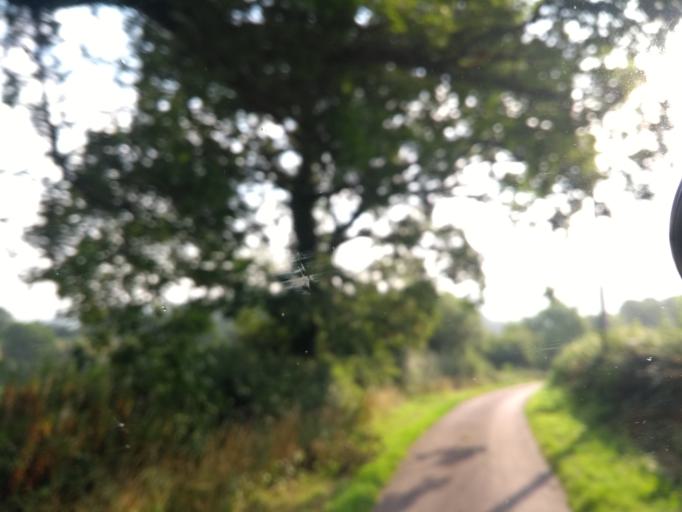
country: GB
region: England
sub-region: Devon
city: Colyton
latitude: 50.7972
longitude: -3.0927
